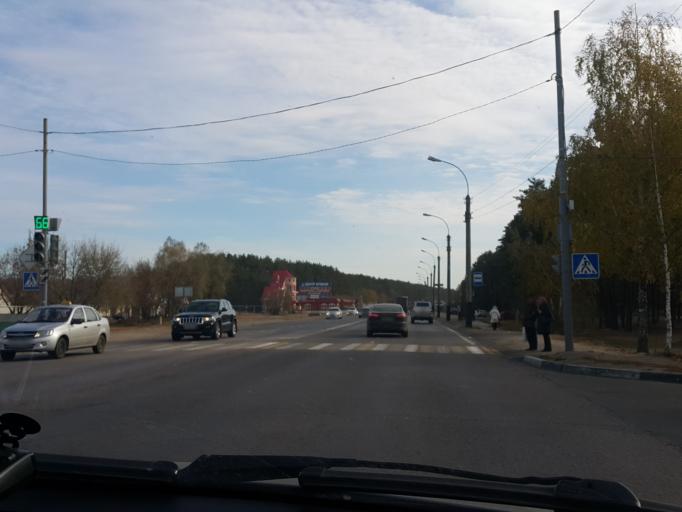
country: RU
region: Tambov
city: Donskoye
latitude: 52.7155
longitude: 41.5095
